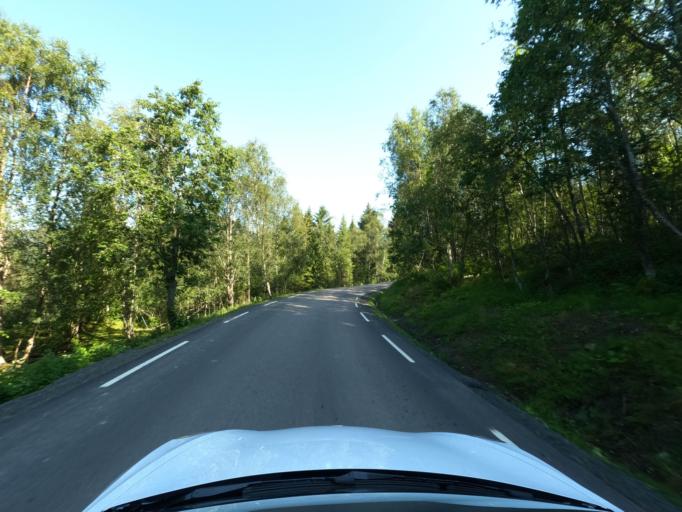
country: NO
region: Nordland
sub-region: Narvik
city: Narvik
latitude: 68.3935
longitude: 17.3069
